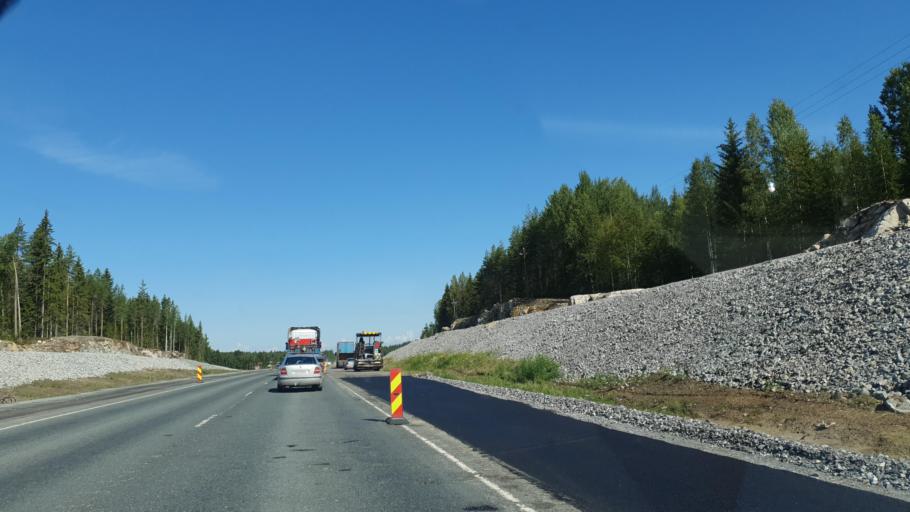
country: FI
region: Northern Savo
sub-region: Ylae-Savo
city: Lapinlahti
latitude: 63.2811
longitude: 27.4562
